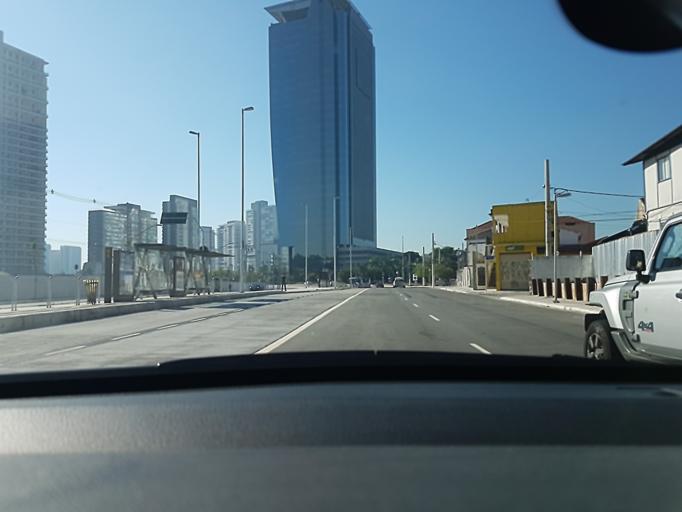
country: BR
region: Sao Paulo
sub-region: Taboao Da Serra
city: Taboao da Serra
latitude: -23.6267
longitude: -46.7052
